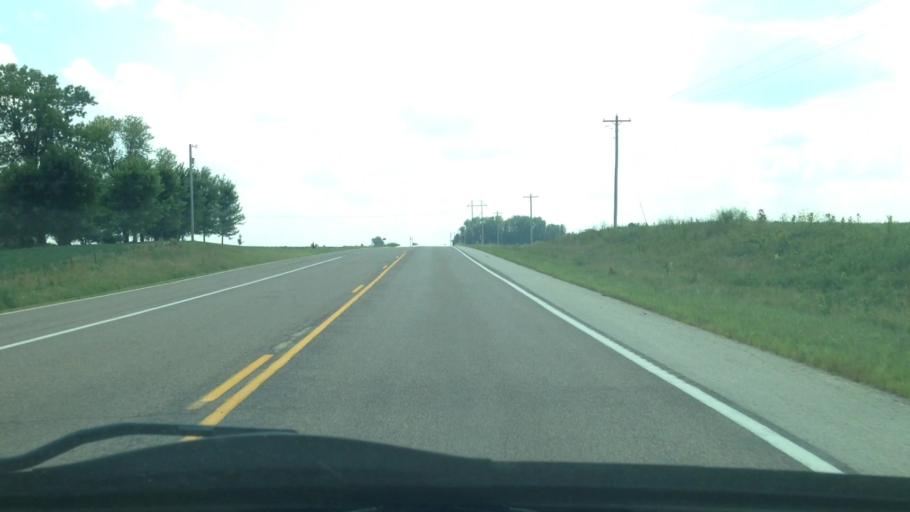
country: US
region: Minnesota
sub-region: Olmsted County
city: Stewartville
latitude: 43.9130
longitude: -92.4085
